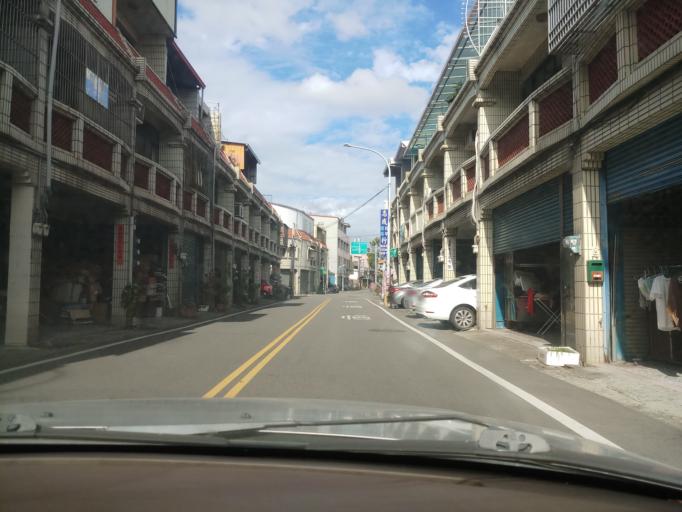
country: TW
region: Taiwan
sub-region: Miaoli
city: Miaoli
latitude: 24.6809
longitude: 120.8627
